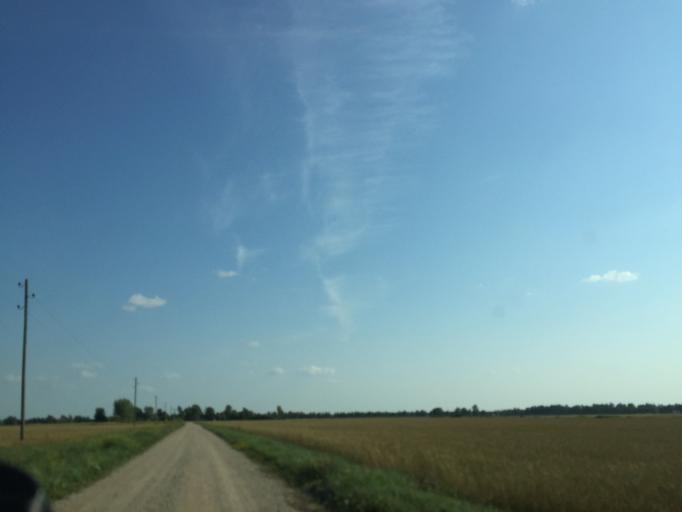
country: LV
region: Jelgava
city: Jelgava
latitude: 56.4599
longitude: 23.6808
